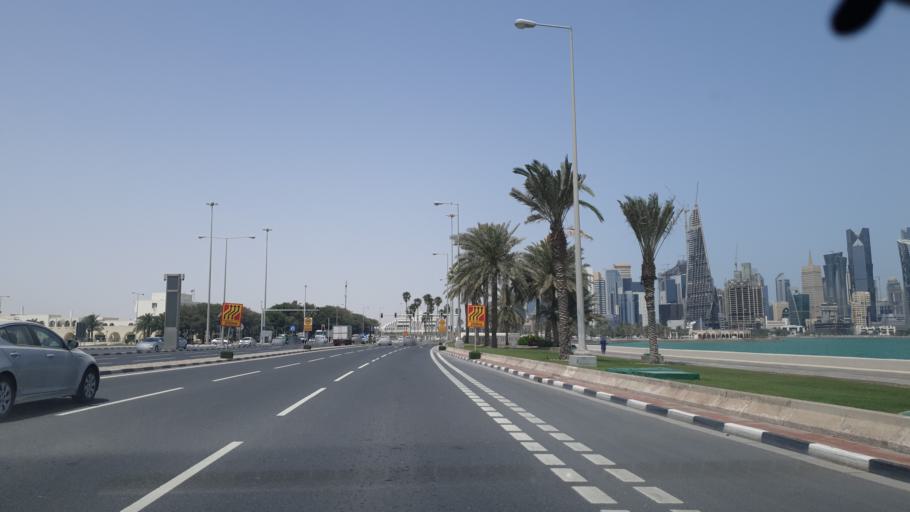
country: QA
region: Baladiyat ad Dawhah
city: Doha
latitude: 25.3027
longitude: 51.5182
